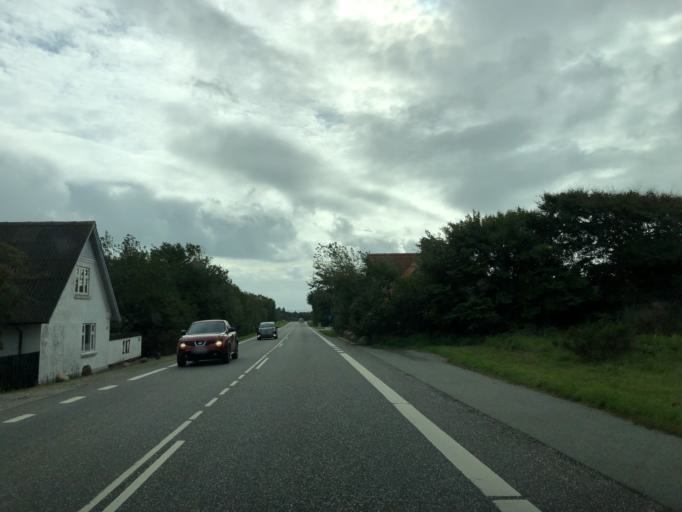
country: DK
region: North Denmark
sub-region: Thisted Kommune
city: Hurup
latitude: 56.6945
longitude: 8.4032
